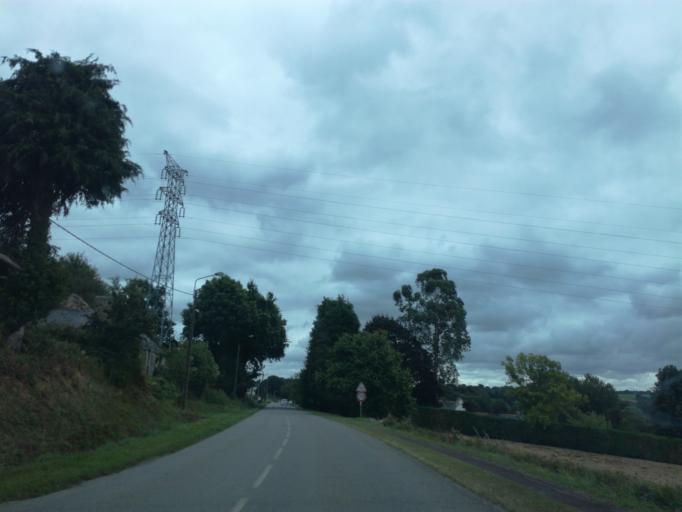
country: FR
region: Brittany
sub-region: Departement du Morbihan
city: Cleguerec
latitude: 48.1187
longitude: -3.0611
